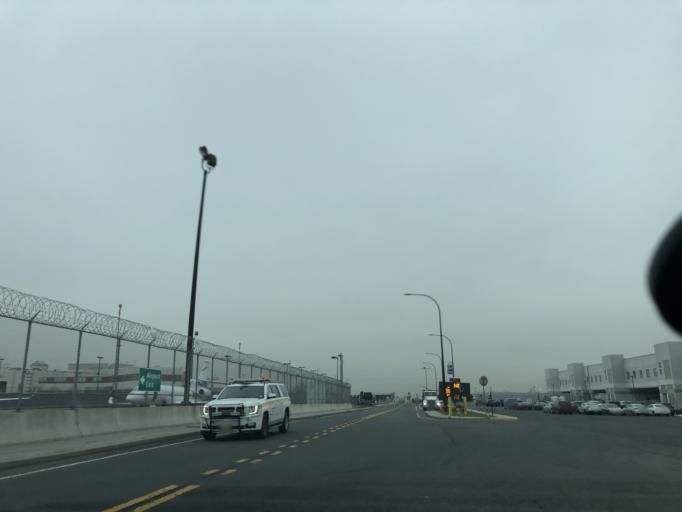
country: US
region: New Jersey
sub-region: Essex County
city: Newark
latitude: 40.7064
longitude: -74.1714
